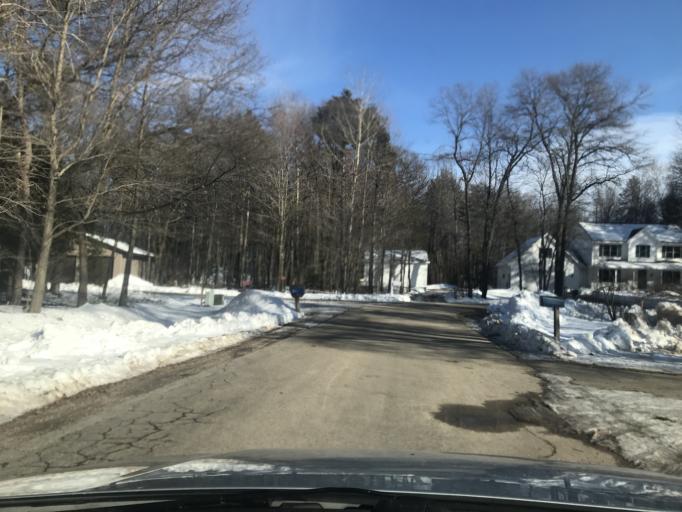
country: US
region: Wisconsin
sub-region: Marinette County
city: Peshtigo
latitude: 45.0294
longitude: -87.7055
